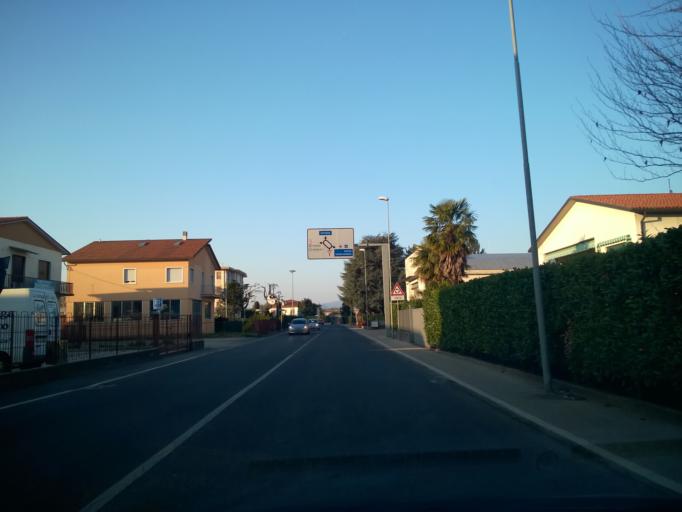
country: IT
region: Veneto
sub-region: Provincia di Vicenza
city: Thiene
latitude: 45.7129
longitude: 11.4682
